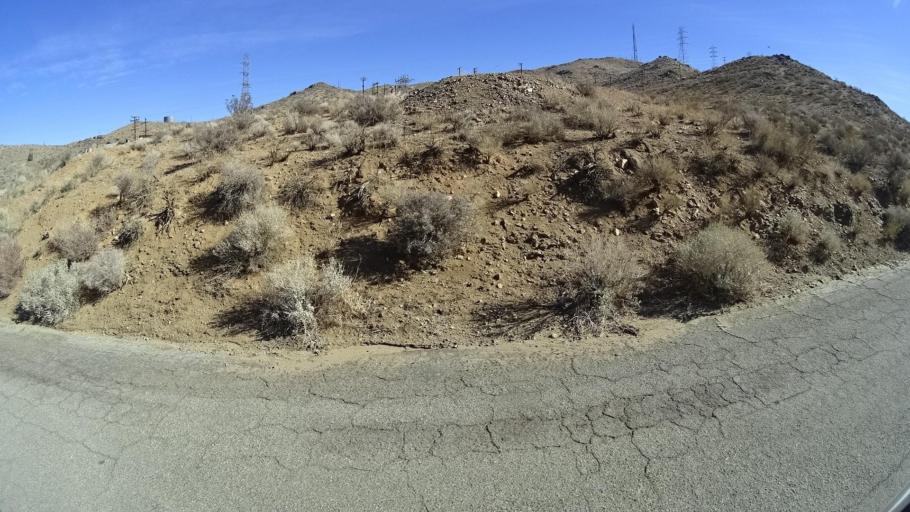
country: US
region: California
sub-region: Kern County
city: Ridgecrest
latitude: 35.3653
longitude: -117.6496
